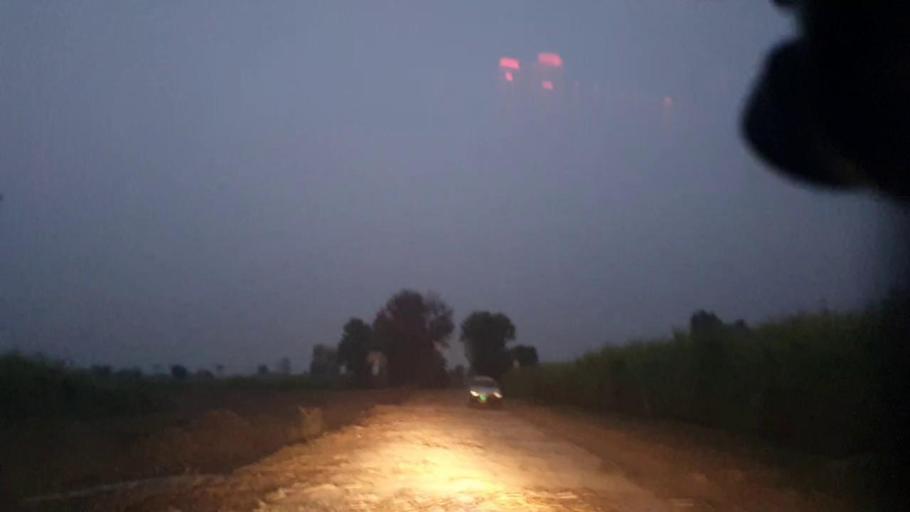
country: PK
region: Sindh
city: Hingorja
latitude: 27.2117
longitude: 68.3732
